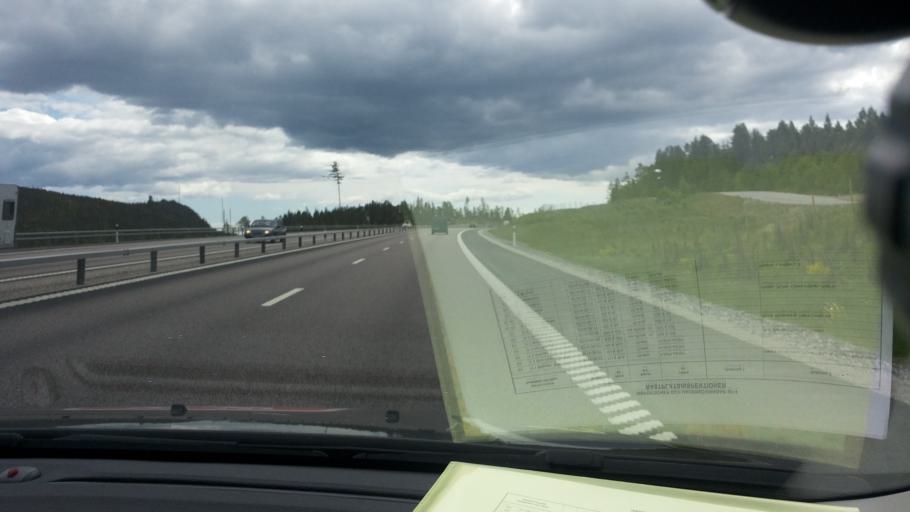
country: SE
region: Vaesternorrland
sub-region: Sundsvalls Kommun
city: Stockvik
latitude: 62.3158
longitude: 17.3403
